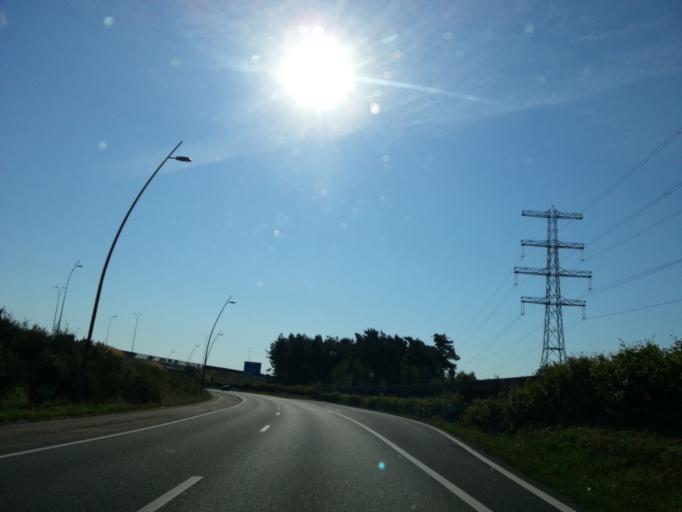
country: NL
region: North Brabant
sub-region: Gemeente Eindhoven
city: Lakerlopen
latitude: 51.4043
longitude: 5.4934
